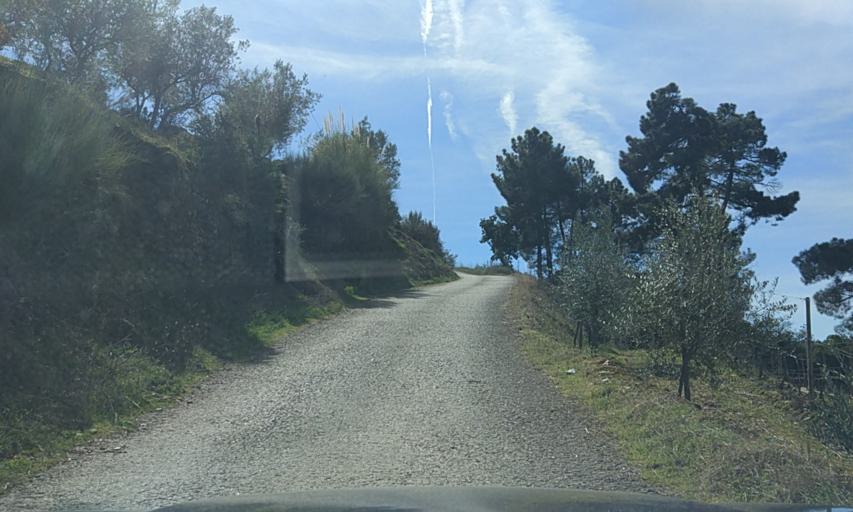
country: PT
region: Vila Real
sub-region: Sabrosa
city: Sabrosa
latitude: 41.3034
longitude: -7.5465
